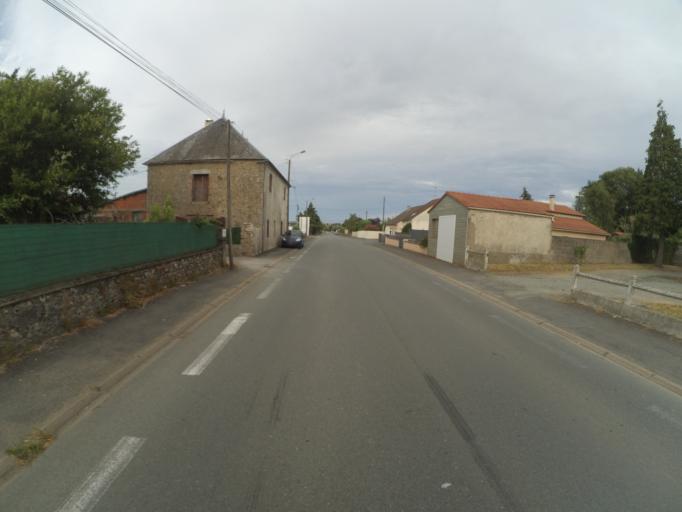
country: FR
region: Poitou-Charentes
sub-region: Departement des Deux-Sevres
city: Saint-Pierre-des-Echaubrognes
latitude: 46.9241
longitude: -0.7423
